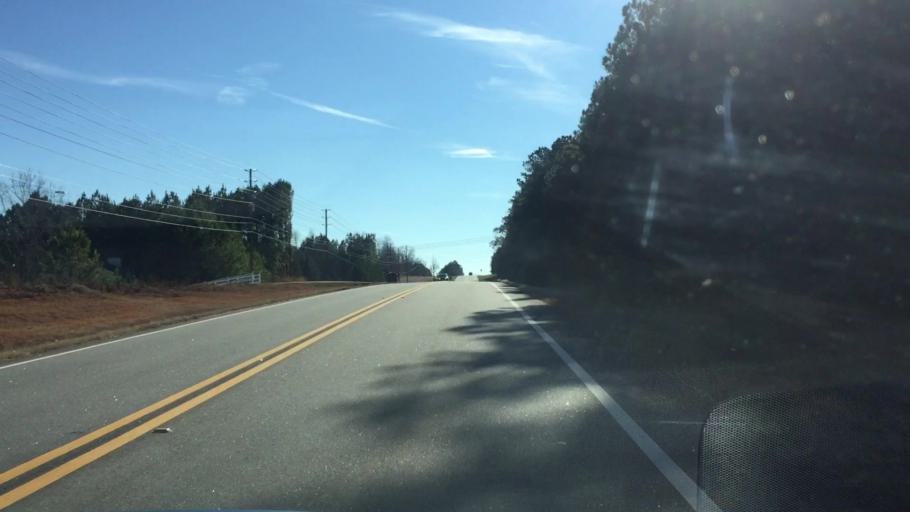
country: US
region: Georgia
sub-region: Newton County
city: Oakwood
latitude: 33.4696
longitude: -83.9655
